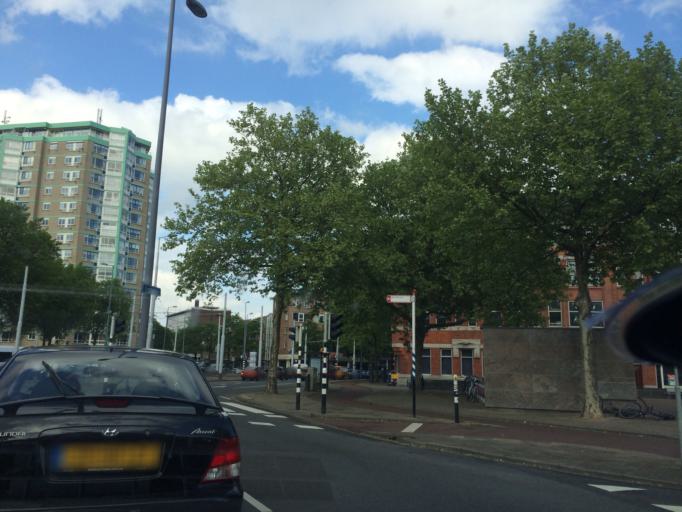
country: NL
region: South Holland
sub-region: Gemeente Rotterdam
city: Rotterdam
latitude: 51.9226
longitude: 4.4971
